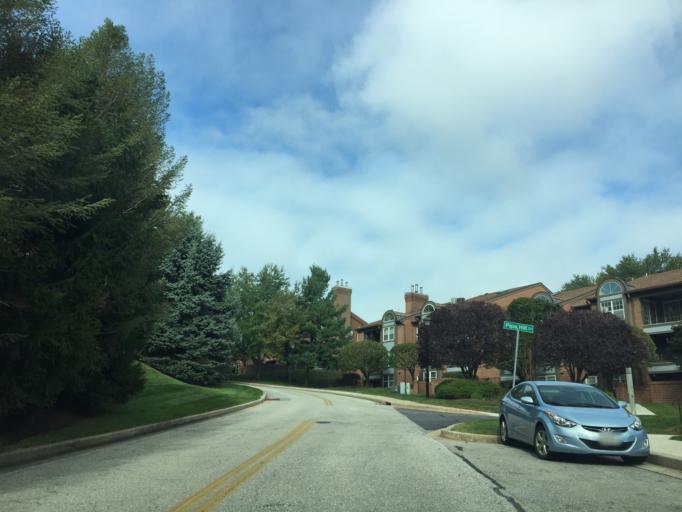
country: US
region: Maryland
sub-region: Baltimore County
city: Pikesville
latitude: 39.3814
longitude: -76.6699
